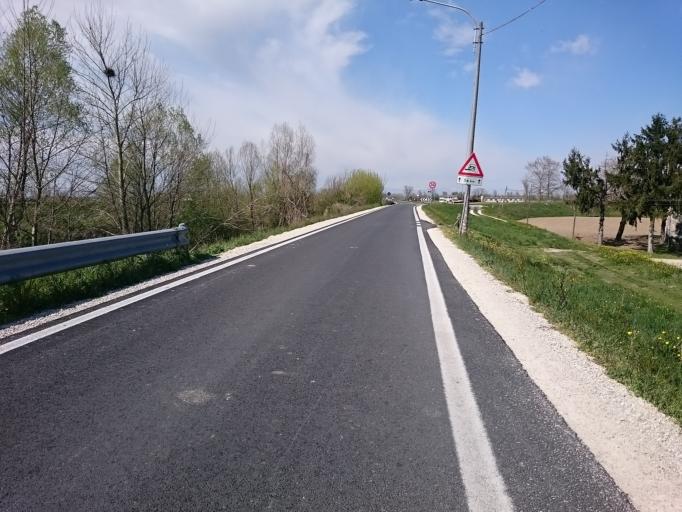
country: IT
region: Veneto
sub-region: Provincia di Padova
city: Polverara
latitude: 45.3224
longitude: 11.9416
